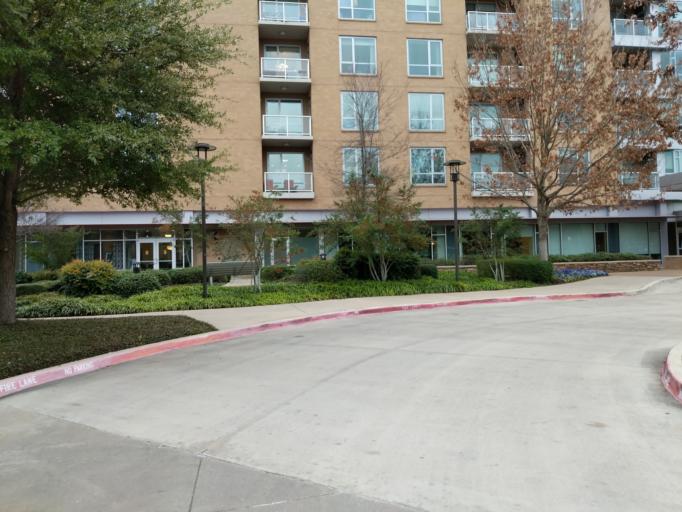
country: US
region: Texas
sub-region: Dallas County
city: Highland Park
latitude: 32.8529
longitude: -96.7312
